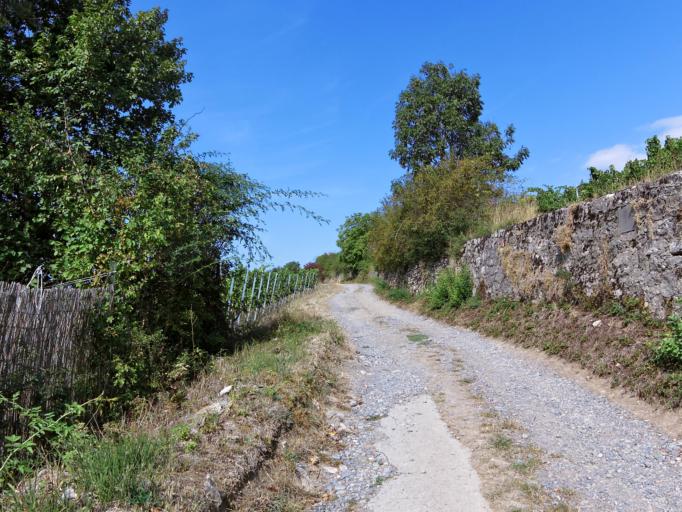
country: DE
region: Bavaria
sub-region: Regierungsbezirk Unterfranken
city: Theilheim
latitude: 49.7549
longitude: 10.0143
